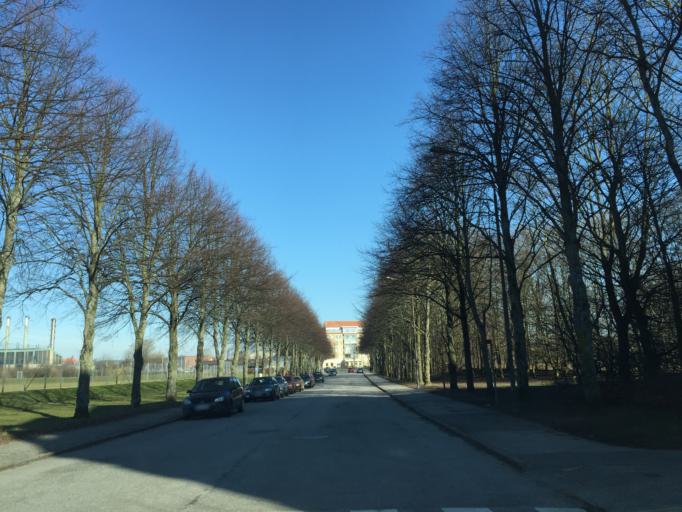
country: SE
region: Skane
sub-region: Lunds Kommun
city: Lund
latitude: 55.6932
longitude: 13.1732
